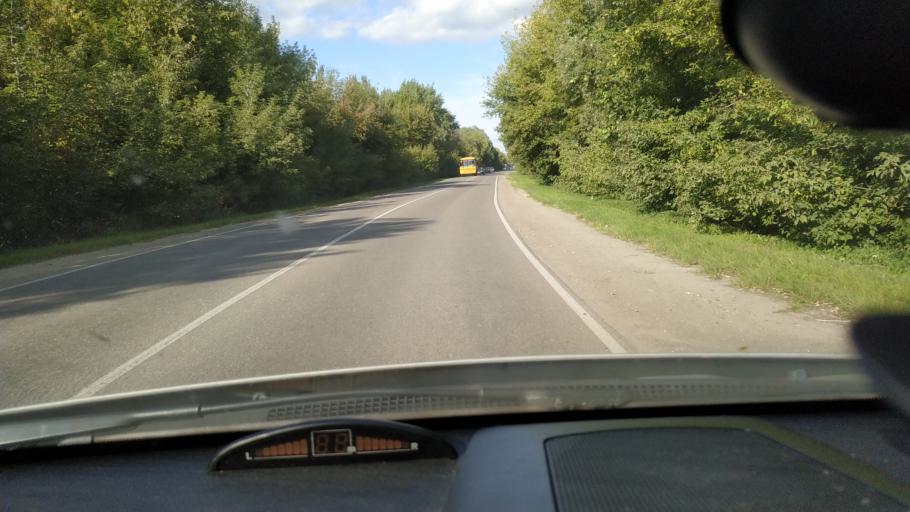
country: RU
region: Rjazan
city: Rybnoye
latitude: 54.7396
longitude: 39.5080
